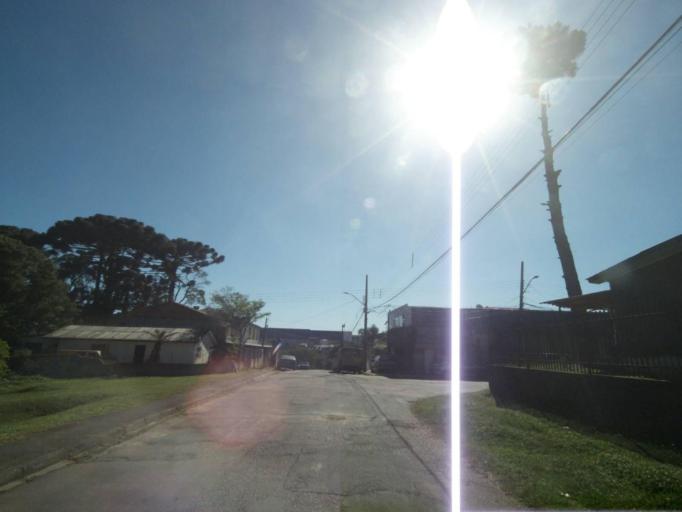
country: BR
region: Parana
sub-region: Curitiba
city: Curitiba
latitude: -25.4544
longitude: -49.3547
